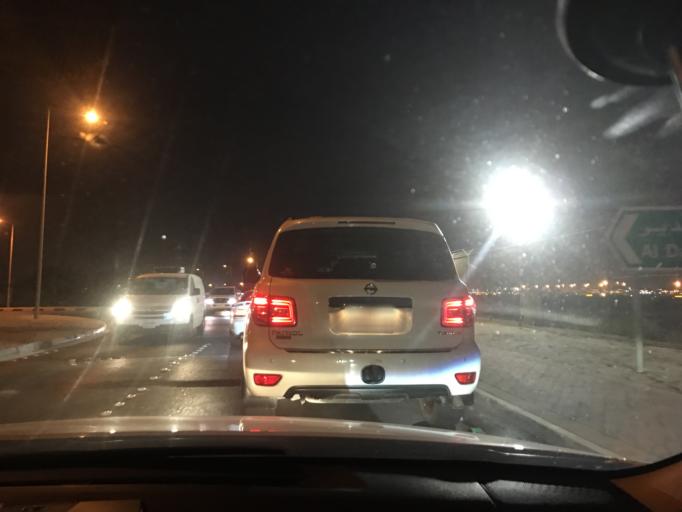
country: BH
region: Muharraq
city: Al Muharraq
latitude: 26.2818
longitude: 50.6182
